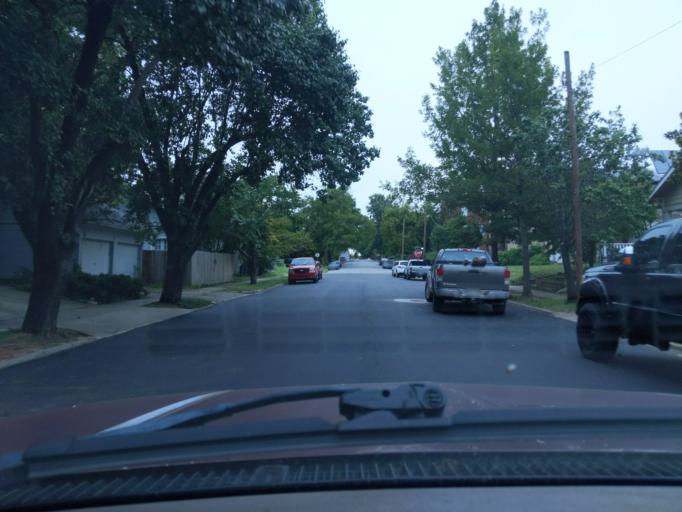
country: US
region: Oklahoma
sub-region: Tulsa County
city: Tulsa
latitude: 36.1362
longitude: -95.9732
